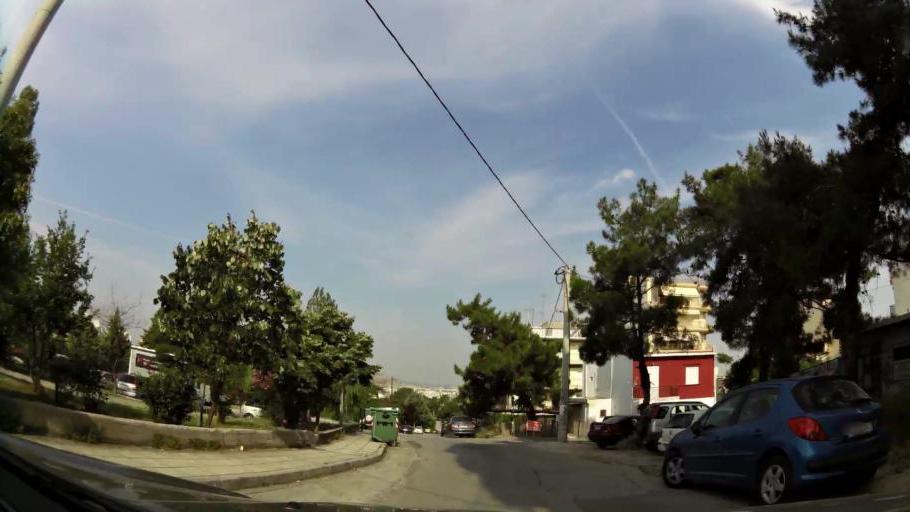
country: GR
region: Central Macedonia
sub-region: Nomos Thessalonikis
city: Polichni
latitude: 40.6577
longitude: 22.9452
